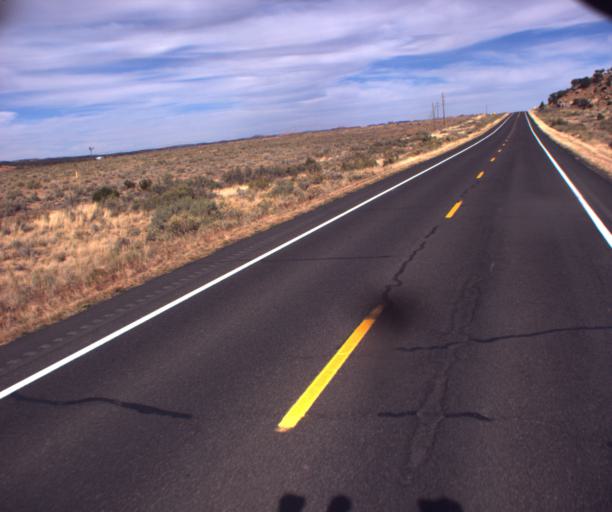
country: US
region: Arizona
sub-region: Navajo County
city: Kayenta
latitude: 36.6714
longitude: -110.4023
